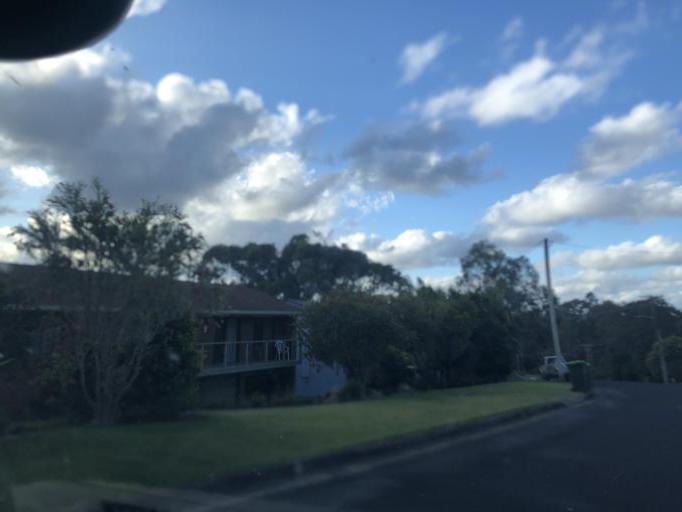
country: AU
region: New South Wales
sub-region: Coffs Harbour
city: Woolgoolga
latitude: -30.0962
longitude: 153.1986
